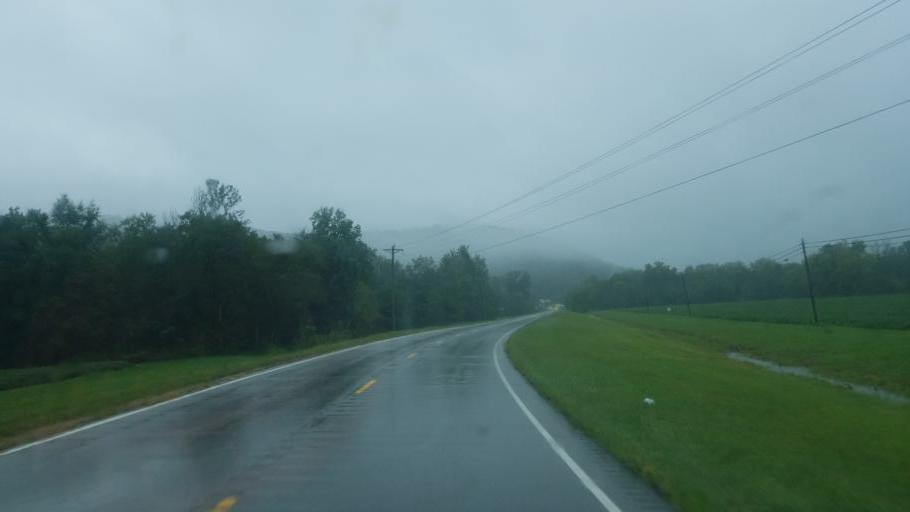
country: US
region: Kentucky
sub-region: Rowan County
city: Morehead
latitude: 38.3139
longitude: -83.5684
